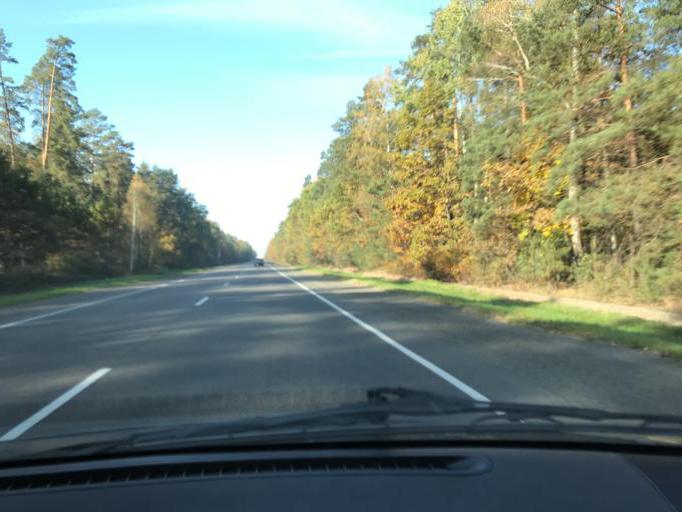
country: BY
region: Brest
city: Horad Luninyets
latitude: 52.2893
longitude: 26.7812
